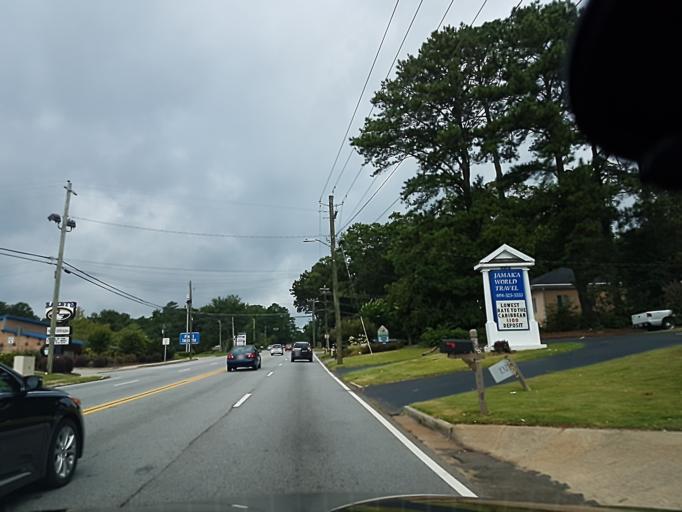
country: US
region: Georgia
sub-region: DeKalb County
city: Scottdale
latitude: 33.8116
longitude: -84.2775
